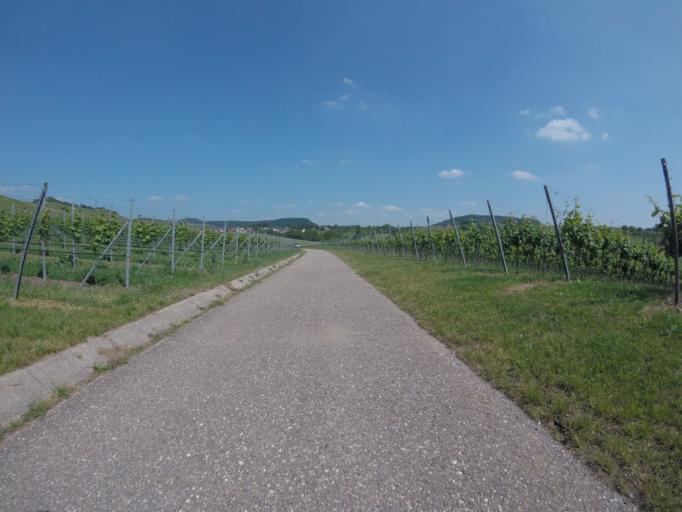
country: DE
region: Baden-Wuerttemberg
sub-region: Regierungsbezirk Stuttgart
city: Abstatt
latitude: 49.0583
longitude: 9.2997
